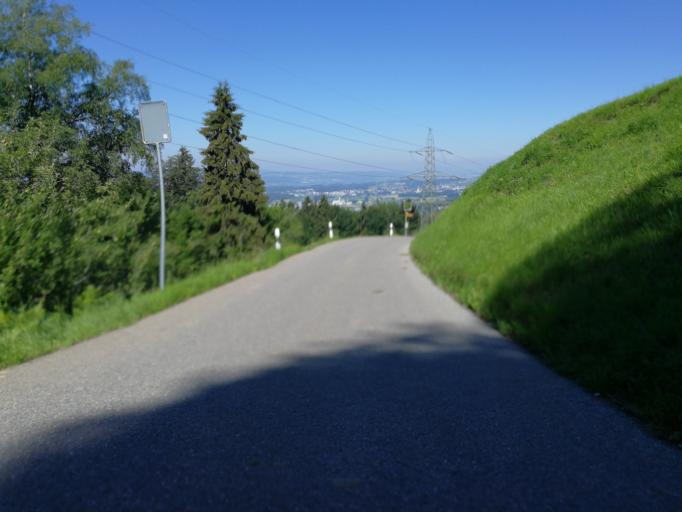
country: CH
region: Zurich
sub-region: Bezirk Hinwil
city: Hadlikon
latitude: 47.2941
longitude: 8.8768
